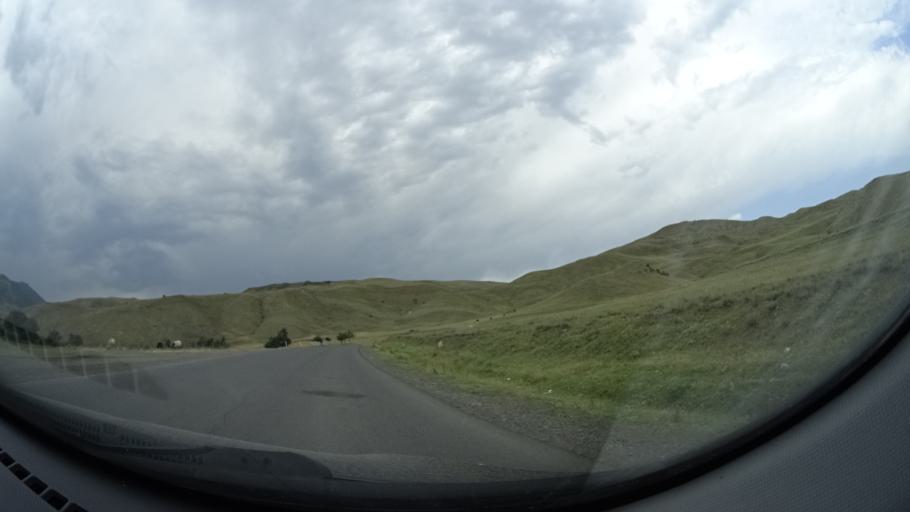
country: GE
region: Samtskhe-Javakheti
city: Aspindza
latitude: 41.5971
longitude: 43.1955
